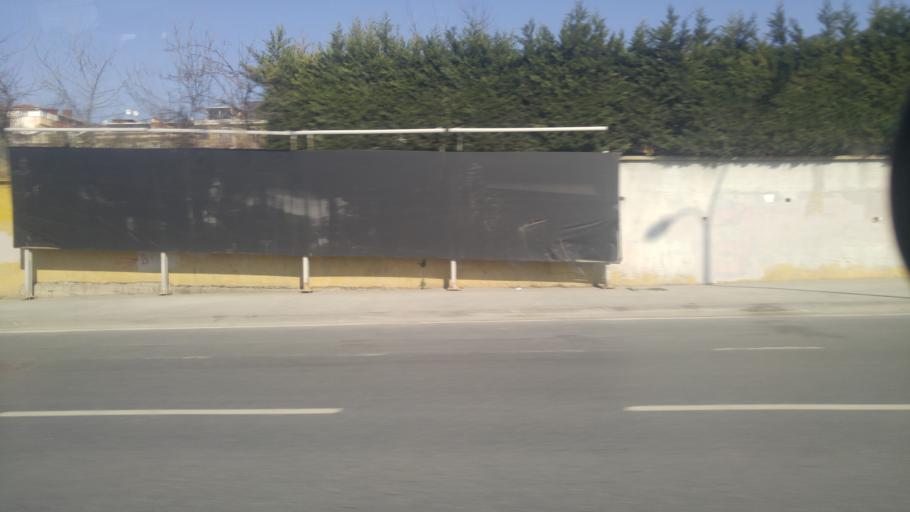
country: TR
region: Istanbul
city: Yakuplu
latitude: 40.9968
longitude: 28.7035
